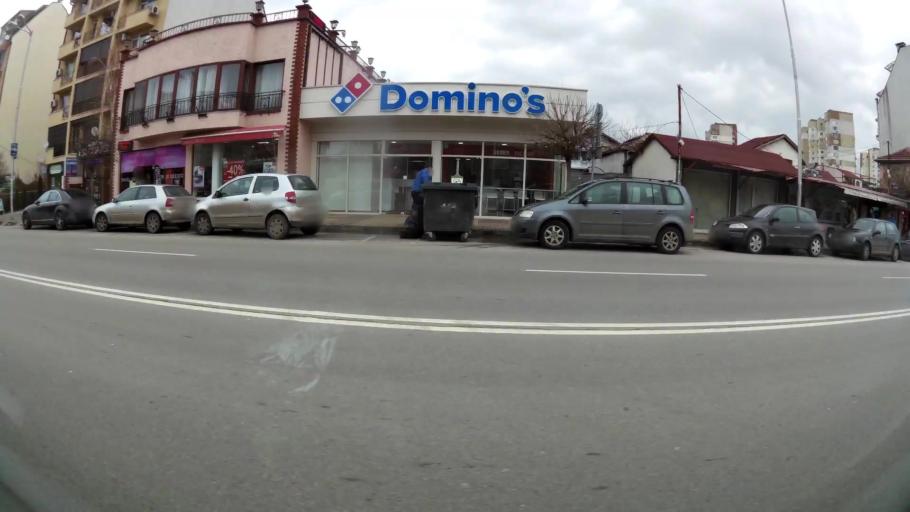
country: BG
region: Sofia-Capital
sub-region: Stolichna Obshtina
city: Sofia
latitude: 42.7342
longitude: 23.2942
